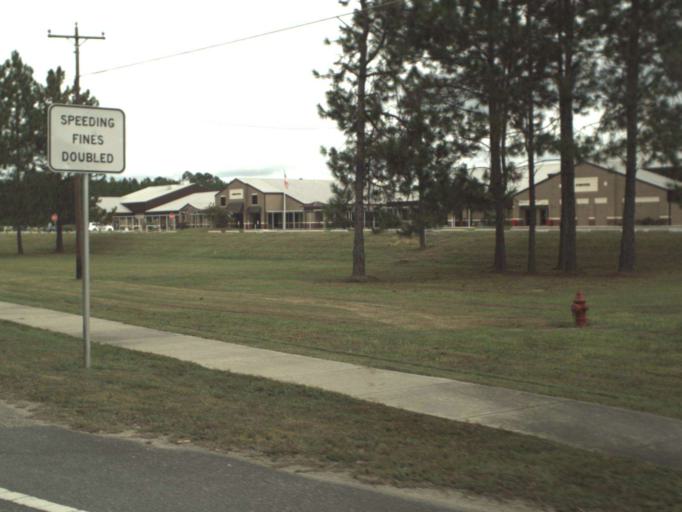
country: US
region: Florida
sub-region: Calhoun County
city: Blountstown
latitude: 30.4677
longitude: -85.0447
